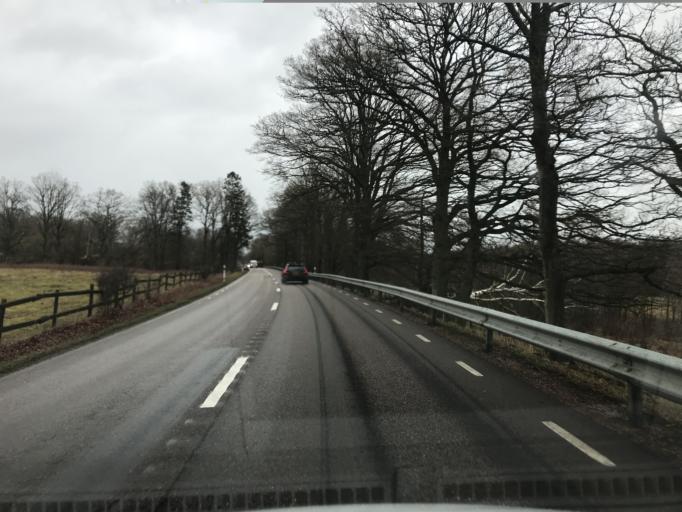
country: SE
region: Skane
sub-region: Klippans Kommun
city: Ljungbyhed
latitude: 56.0921
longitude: 13.2089
